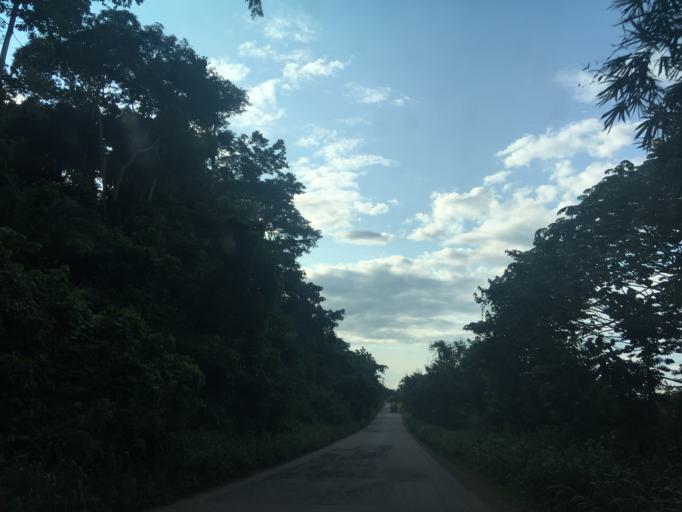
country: GH
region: Western
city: Bibiani
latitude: 6.2803
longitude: -2.2254
